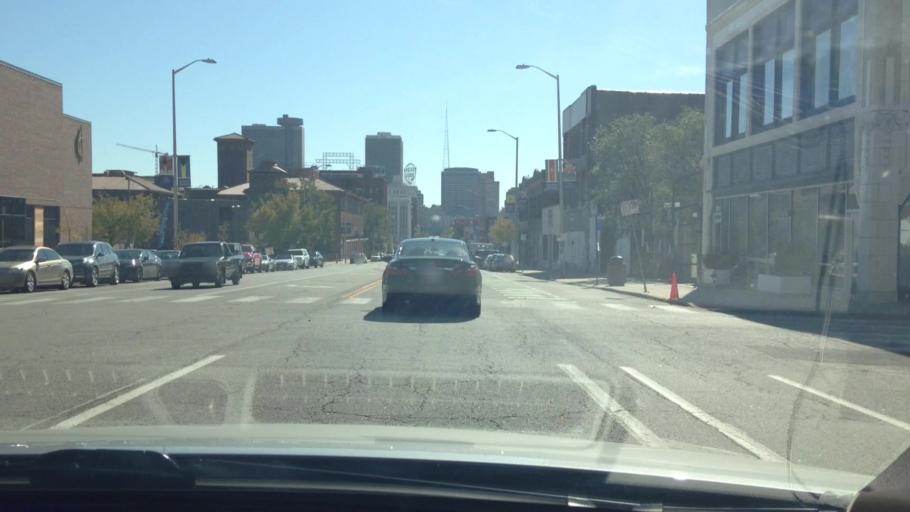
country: US
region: Missouri
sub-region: Jackson County
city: Kansas City
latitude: 39.0946
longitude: -94.5812
